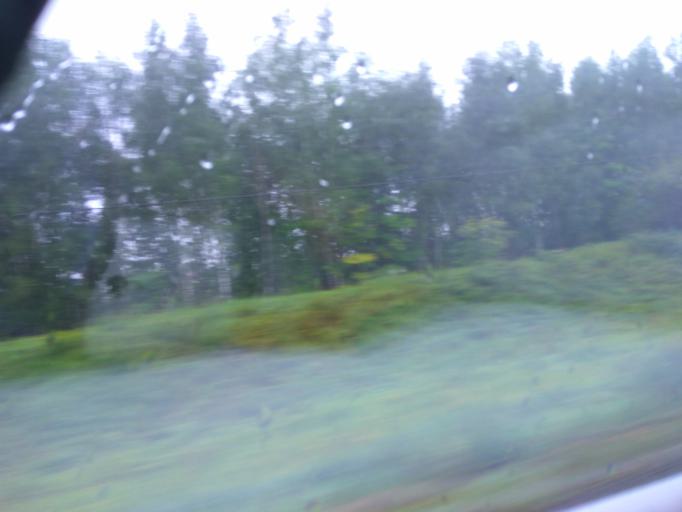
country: RU
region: Moskovskaya
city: Uzunovo
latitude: 54.6361
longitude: 38.5763
